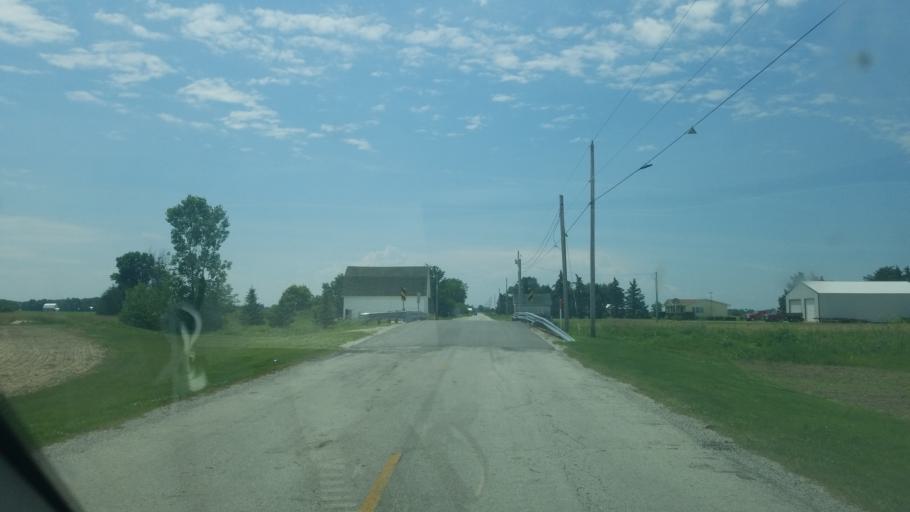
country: US
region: Ohio
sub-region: Wood County
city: North Baltimore
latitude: 41.2191
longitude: -83.5923
